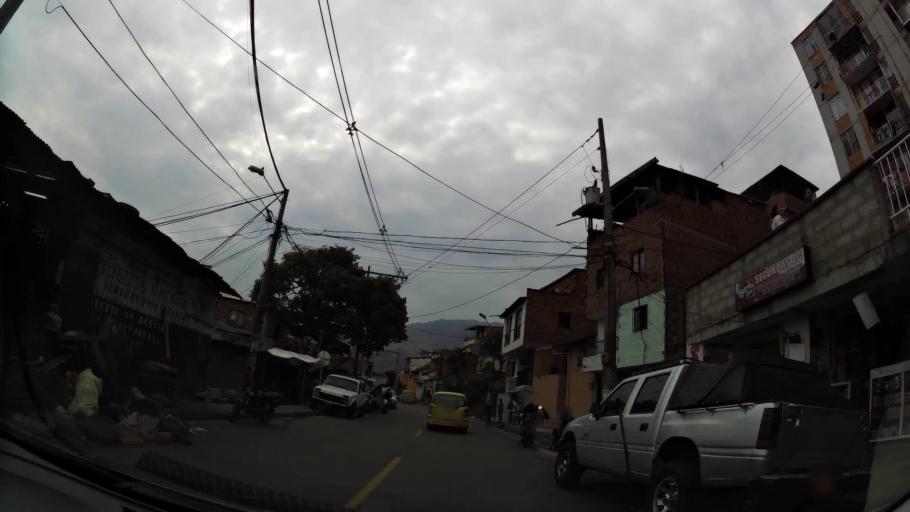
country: CO
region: Antioquia
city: Medellin
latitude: 6.2806
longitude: -75.5649
